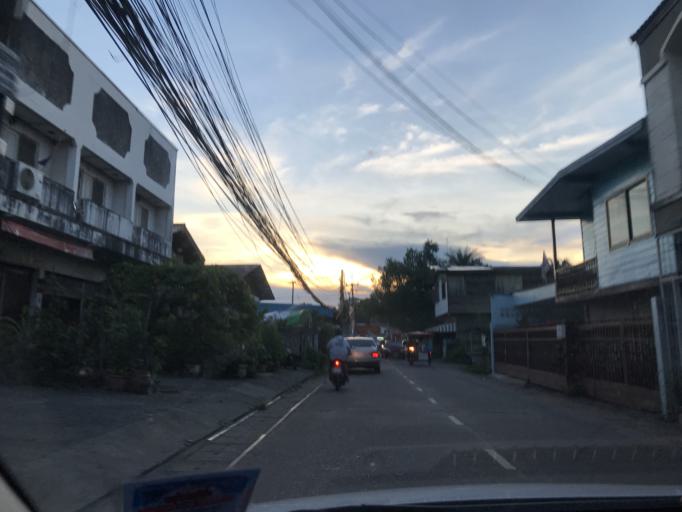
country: TH
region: Changwat Udon Thani
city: Udon Thani
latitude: 17.3970
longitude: 102.7885
